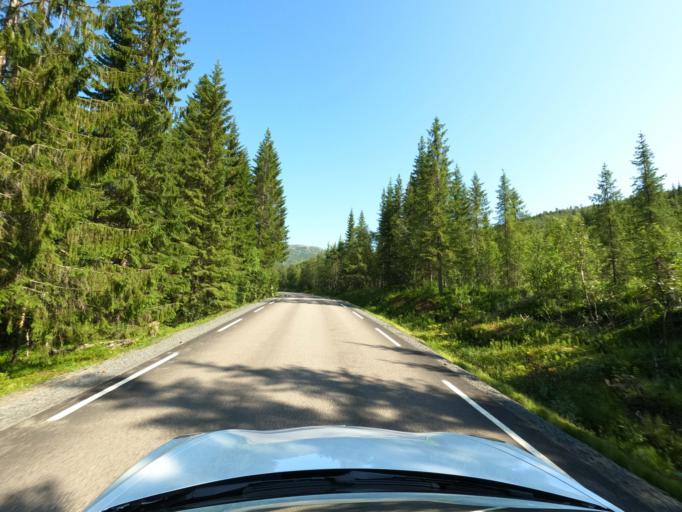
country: NO
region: Nordland
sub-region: Narvik
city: Narvik
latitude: 68.3932
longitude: 17.3246
